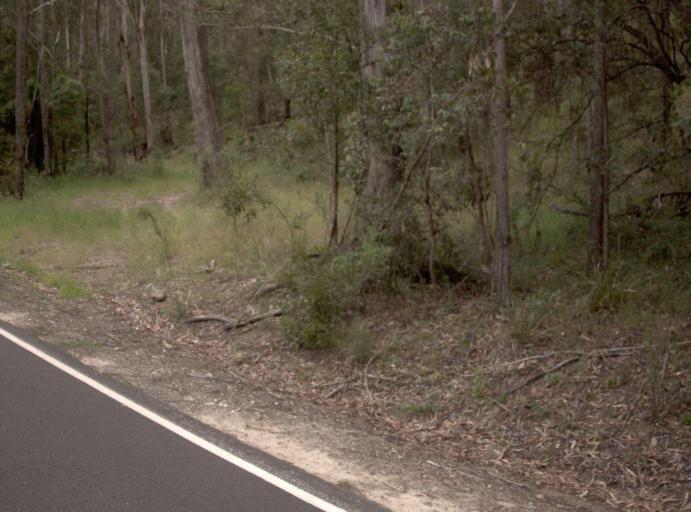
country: AU
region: New South Wales
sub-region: Bombala
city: Bombala
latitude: -37.4445
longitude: 149.1943
